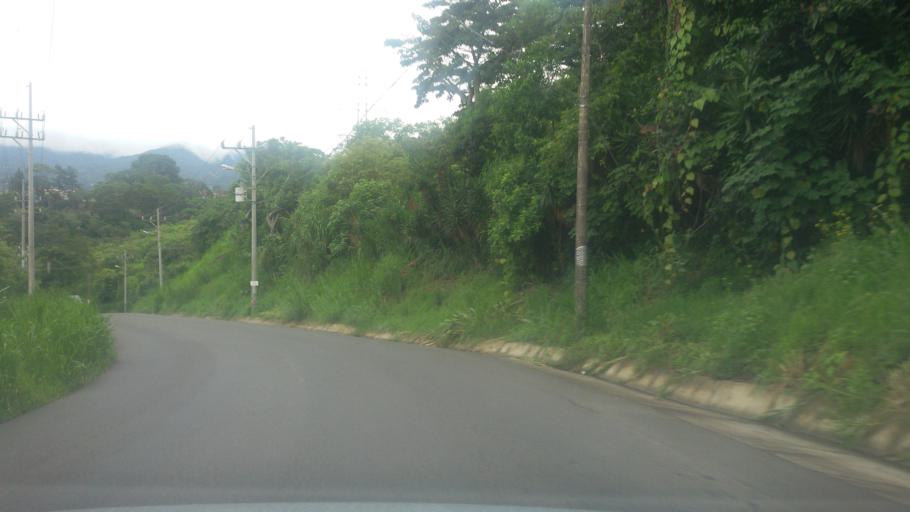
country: CR
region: Heredia
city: Angeles
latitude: 9.9827
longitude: -84.0575
